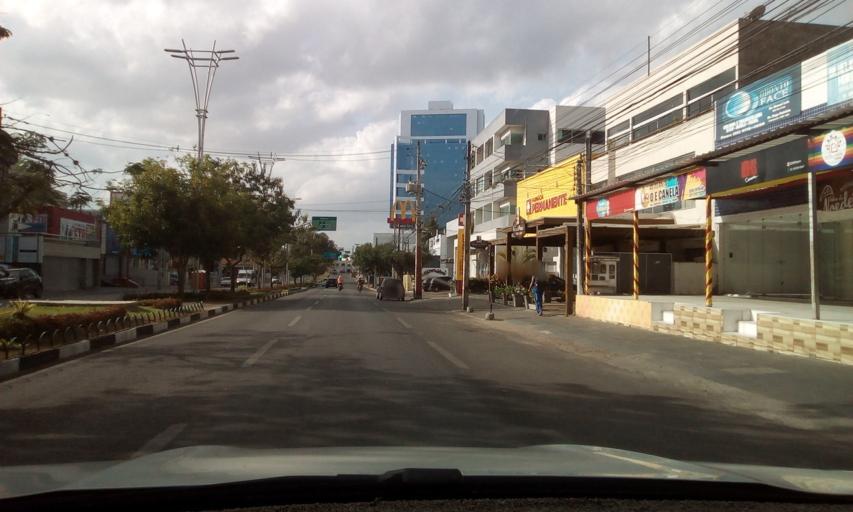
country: BR
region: Pernambuco
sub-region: Caruaru
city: Caruaru
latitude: -8.2732
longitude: -35.9744
